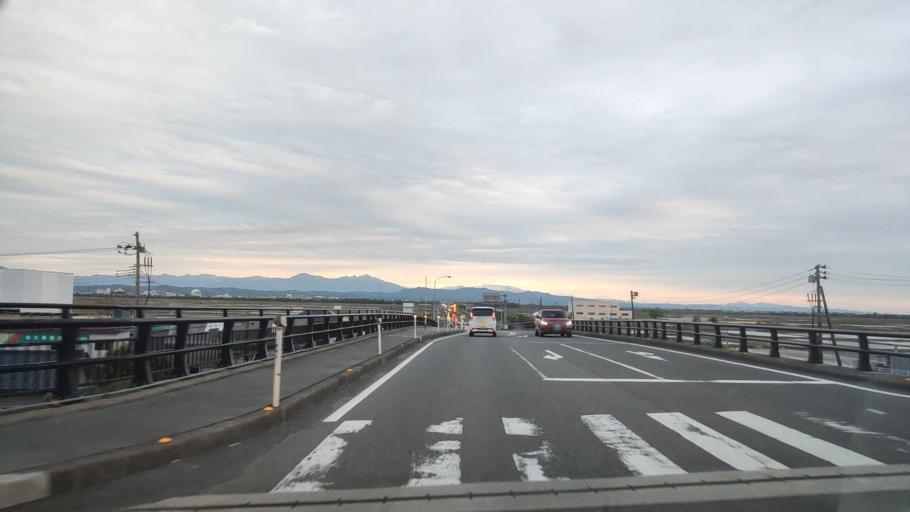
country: JP
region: Niigata
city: Kameda-honcho
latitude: 37.8351
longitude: 139.0964
